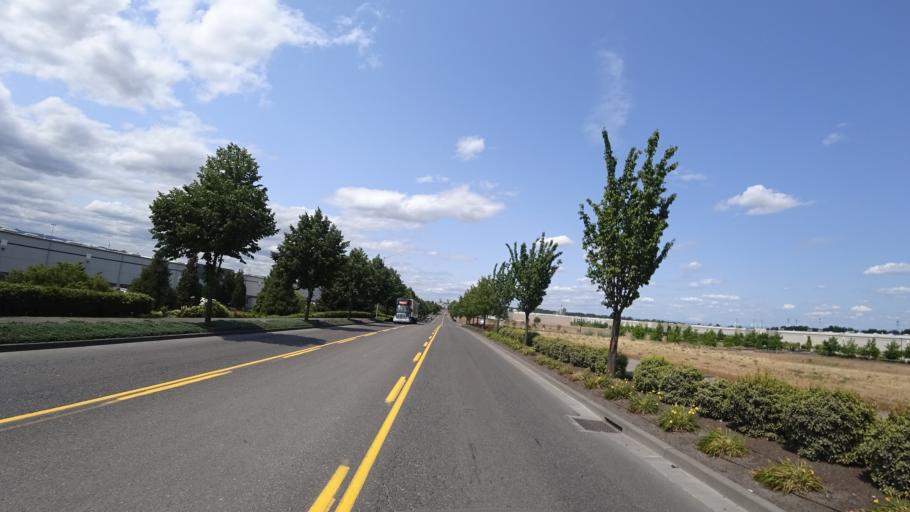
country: US
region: Washington
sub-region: Clark County
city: Lake Shore
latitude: 45.6262
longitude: -122.7717
